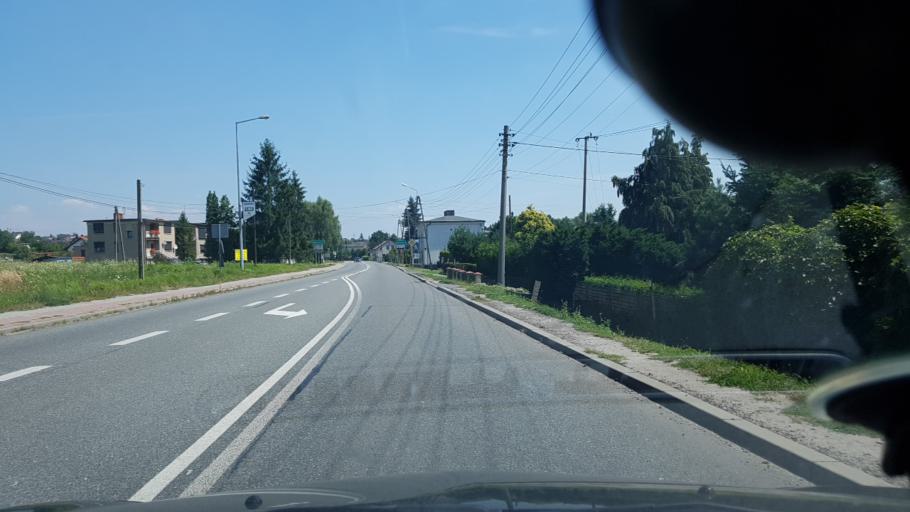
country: PL
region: Silesian Voivodeship
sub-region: Powiat wodzislawski
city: Marklowice
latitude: 50.0160
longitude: 18.4955
